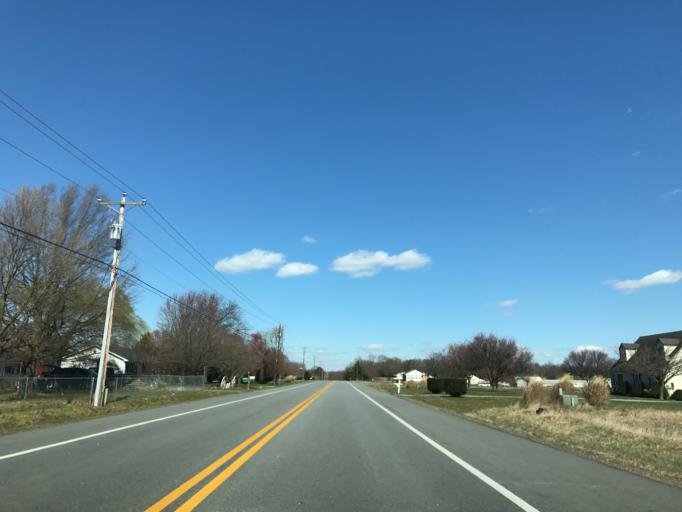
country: US
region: Maryland
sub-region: Queen Anne's County
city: Kingstown
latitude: 39.2428
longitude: -75.8674
